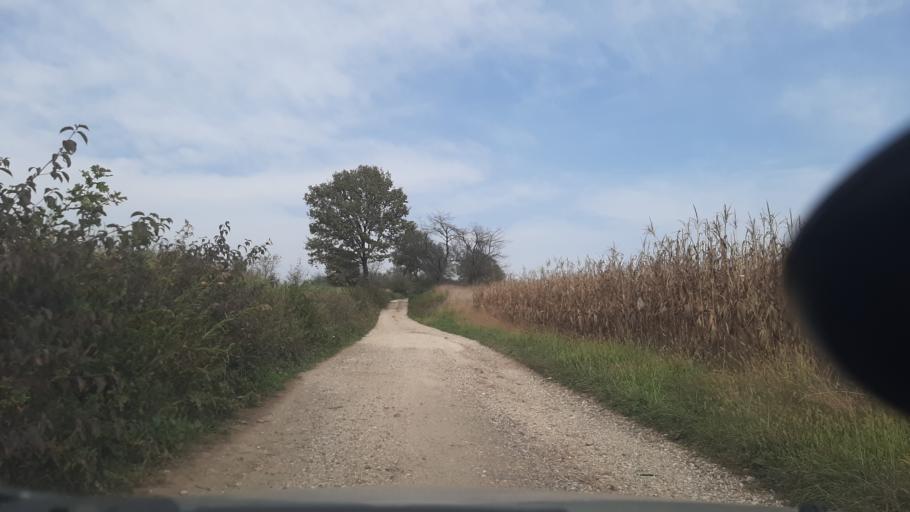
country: BA
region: Republika Srpska
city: Maglajani
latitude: 44.8737
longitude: 17.4715
